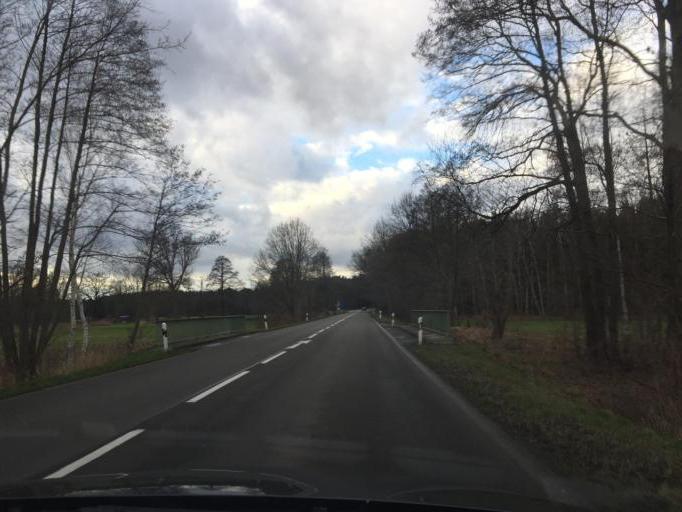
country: DE
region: Brandenburg
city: Kolkwitz
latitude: 51.7508
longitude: 14.2077
